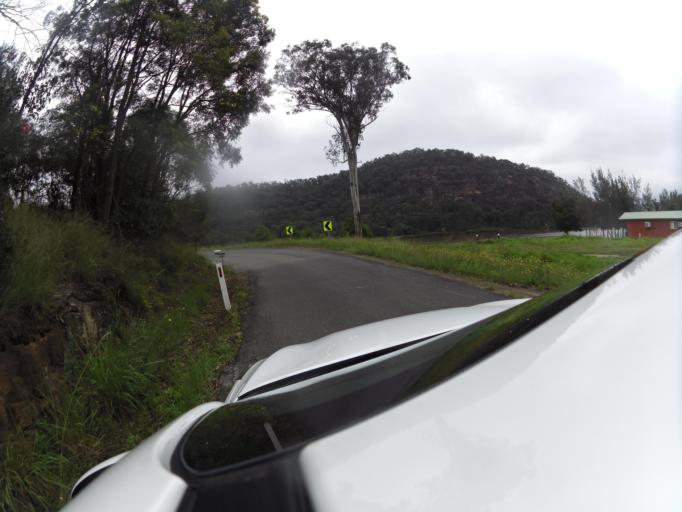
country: AU
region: New South Wales
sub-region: Hornsby Shire
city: Glenorie
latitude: -33.4036
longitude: 150.9747
